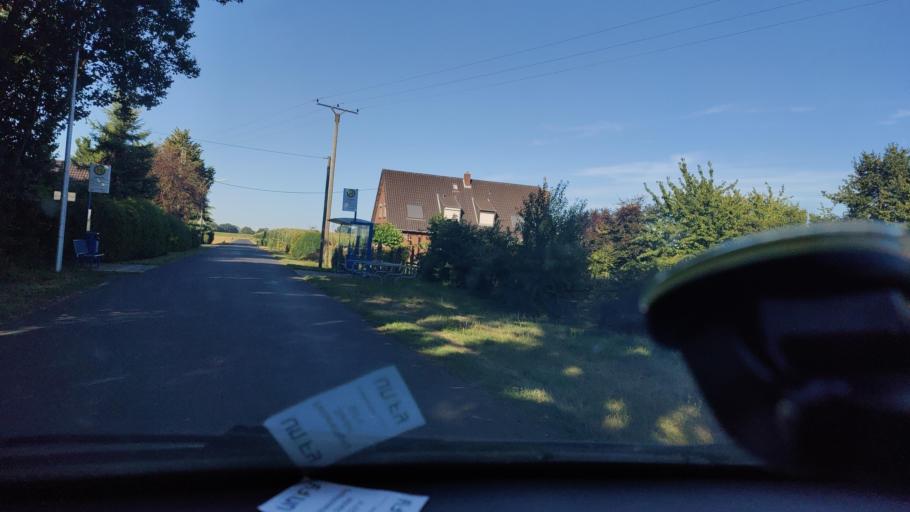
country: DE
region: North Rhine-Westphalia
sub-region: Regierungsbezirk Dusseldorf
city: Goch
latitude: 51.6642
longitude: 6.1088
